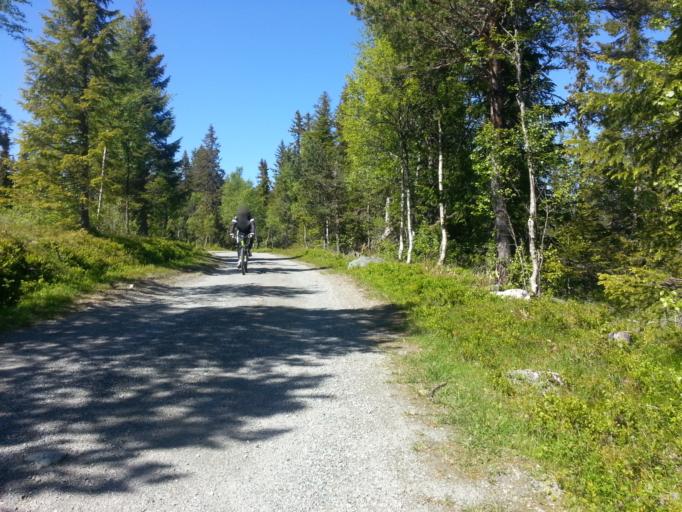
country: NO
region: Sor-Trondelag
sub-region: Trondheim
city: Trondheim
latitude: 63.4116
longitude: 10.2837
